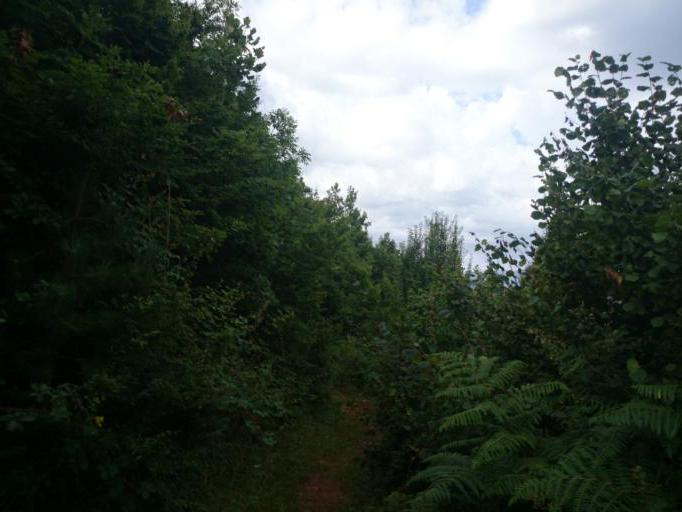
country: AL
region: Elbasan
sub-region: Rrethi i Gramshit
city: Lenias
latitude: 40.7705
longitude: 20.3380
